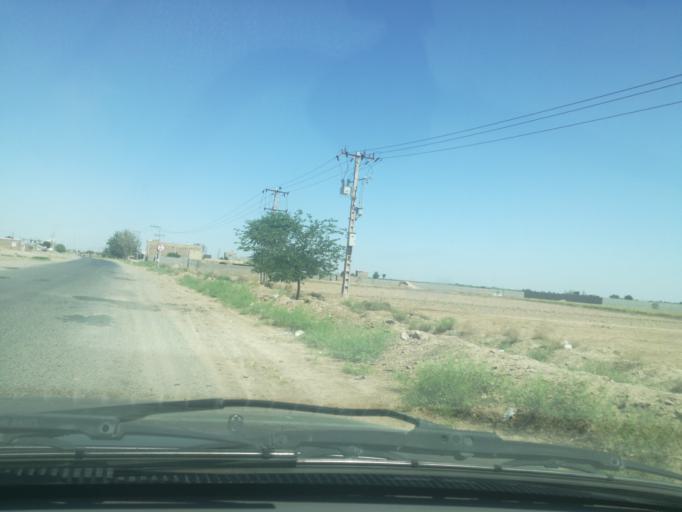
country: IR
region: Razavi Khorasan
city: Sarakhs
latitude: 36.5620
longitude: 61.1475
